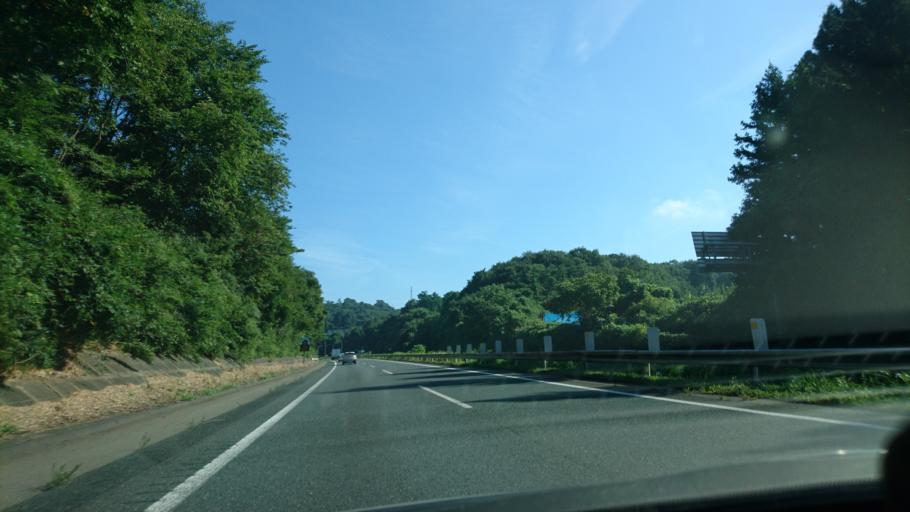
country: JP
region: Iwate
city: Ichinoseki
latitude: 38.9434
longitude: 141.1035
